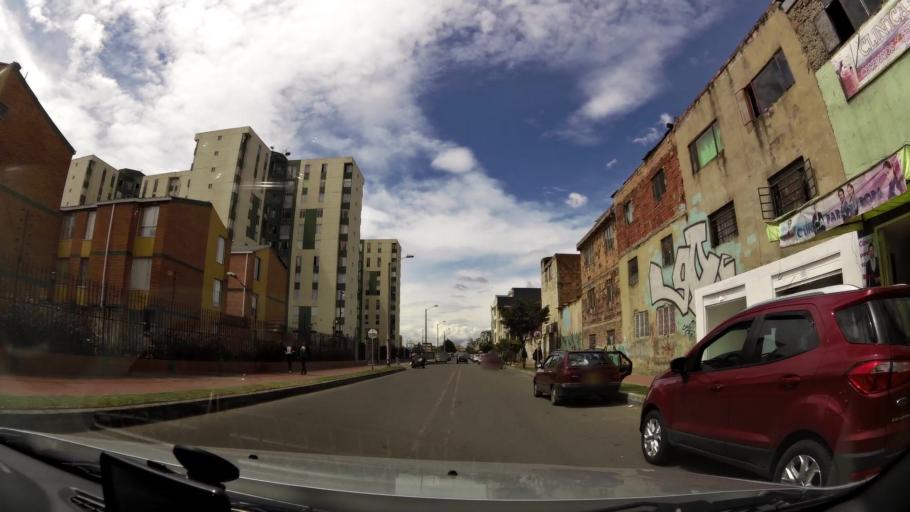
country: CO
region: Bogota D.C.
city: Bogota
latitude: 4.6184
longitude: -74.1296
